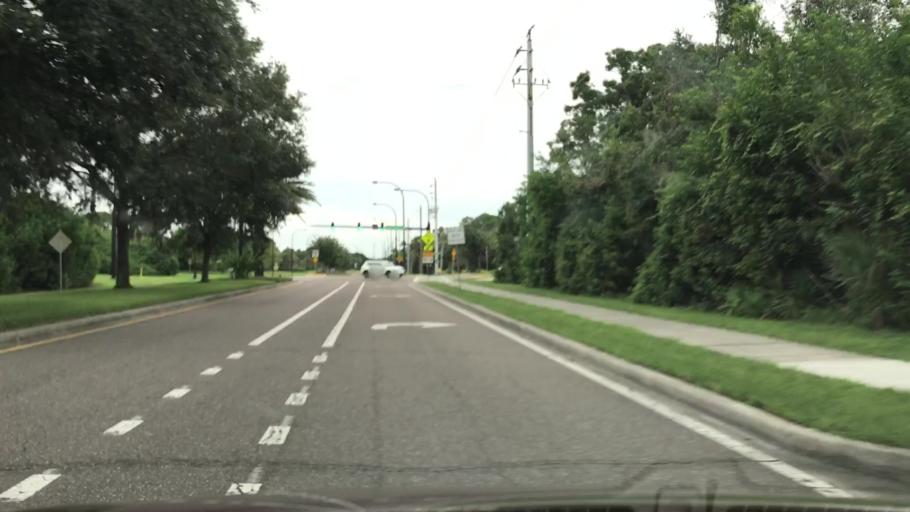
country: US
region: Florida
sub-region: Sarasota County
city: Vamo
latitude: 27.2437
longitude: -82.4745
